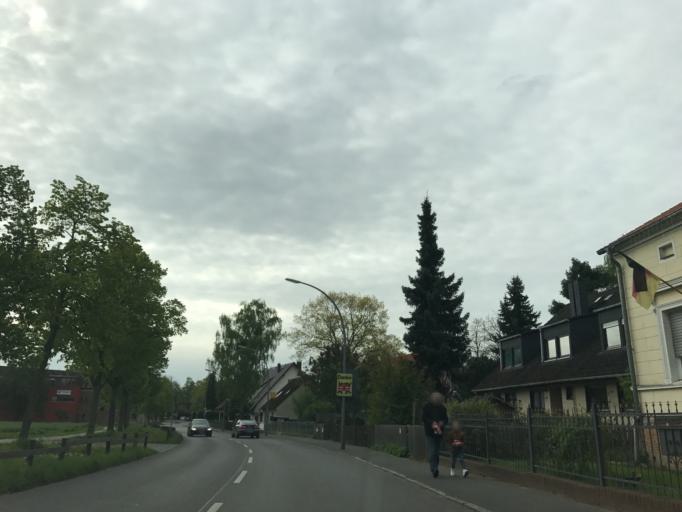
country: DE
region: Berlin
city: Kladow
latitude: 52.4558
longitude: 13.1412
